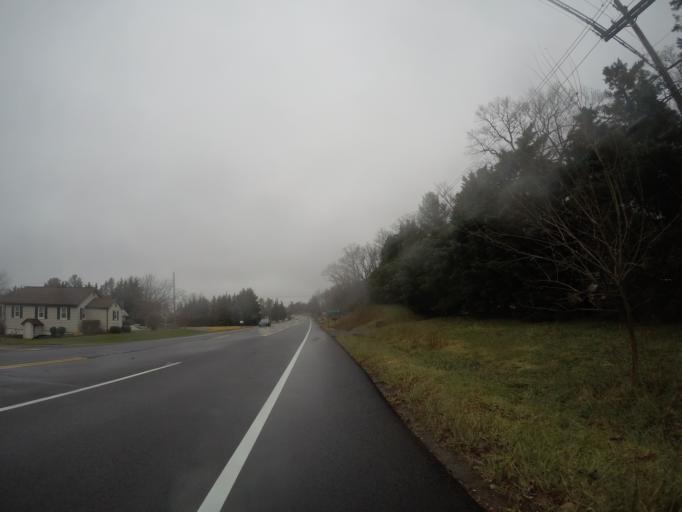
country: US
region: Maryland
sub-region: Howard County
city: Ellicott City
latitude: 39.2319
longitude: -76.7988
